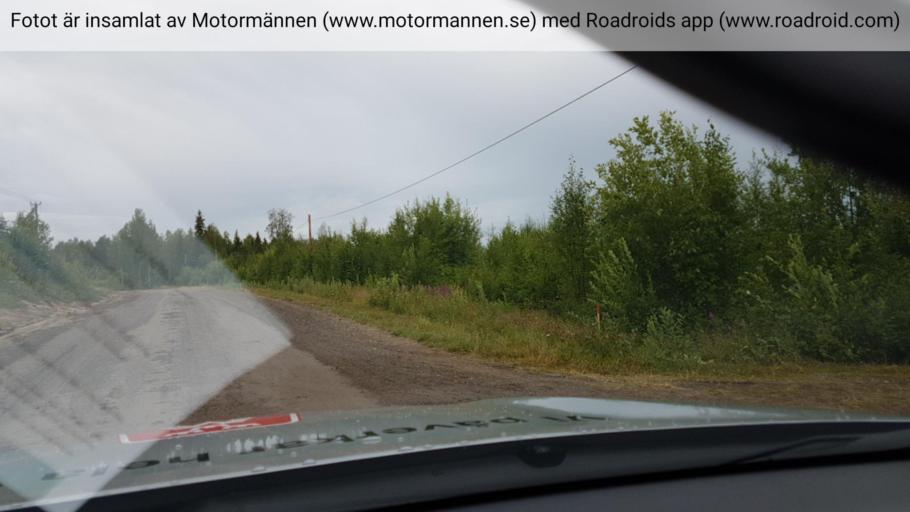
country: SE
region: Norrbotten
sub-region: Alvsbyns Kommun
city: AElvsbyn
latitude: 66.0042
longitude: 21.1293
